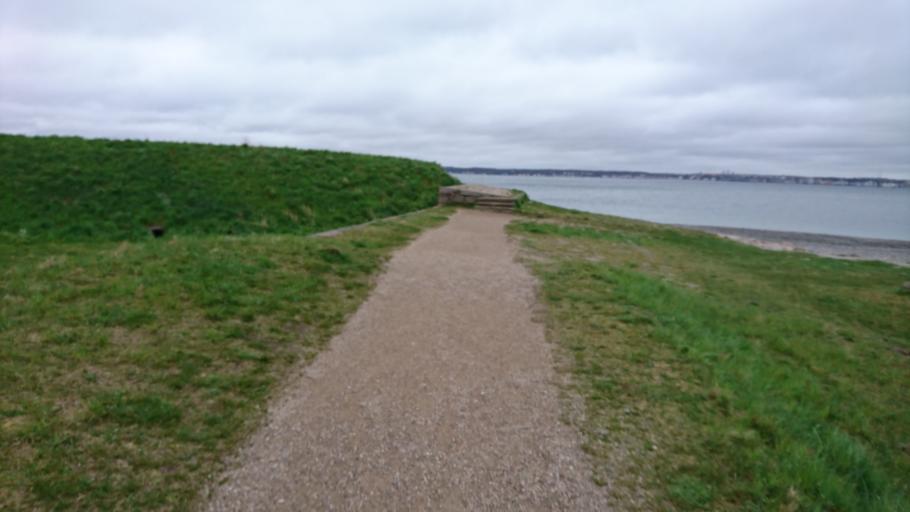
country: DK
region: Capital Region
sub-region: Helsingor Kommune
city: Helsingor
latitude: 56.0388
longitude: 12.6236
